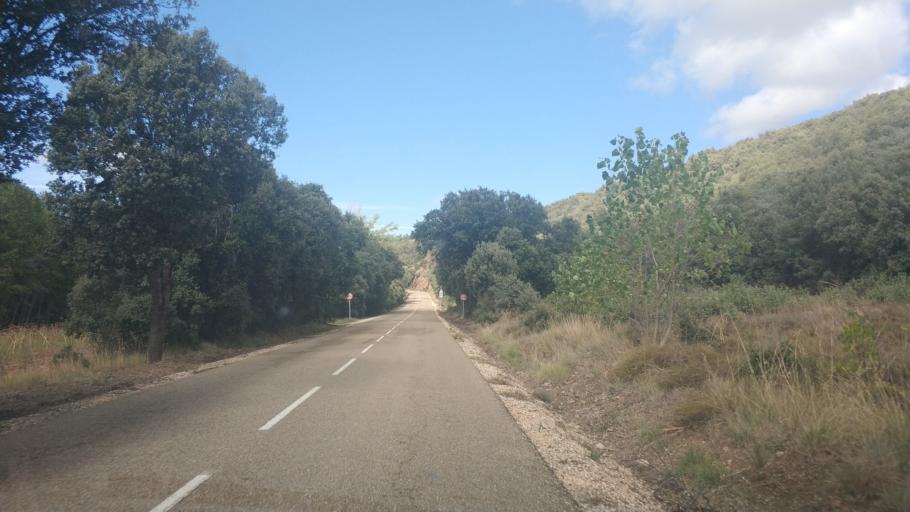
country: ES
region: Castille and Leon
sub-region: Provincia de Burgos
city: Retuerta
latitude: 42.0400
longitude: -3.4876
